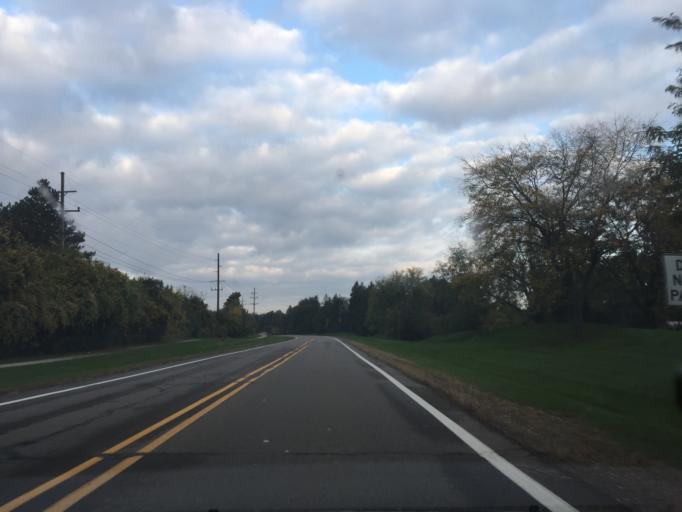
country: US
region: Michigan
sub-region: Oakland County
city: Sylvan Lake
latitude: 42.5834
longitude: -83.3182
